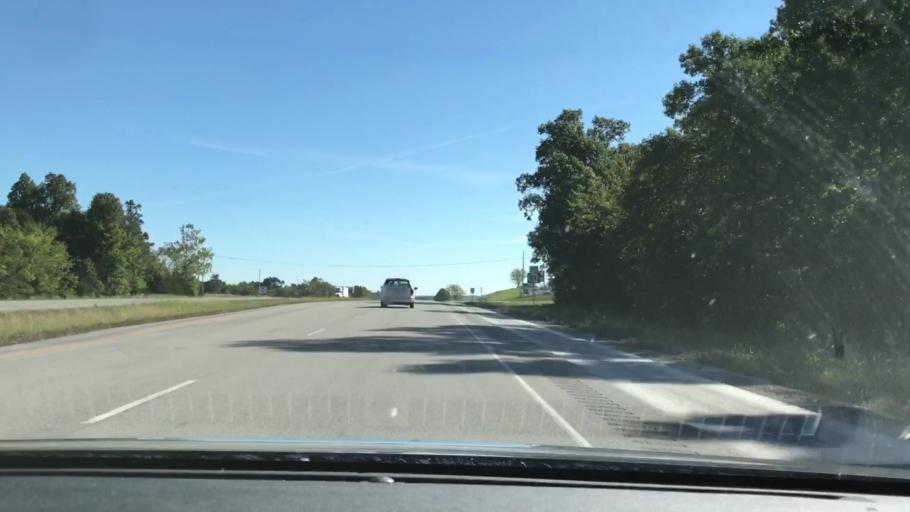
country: US
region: Kentucky
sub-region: Todd County
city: Elkton
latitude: 36.8473
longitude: -87.3134
